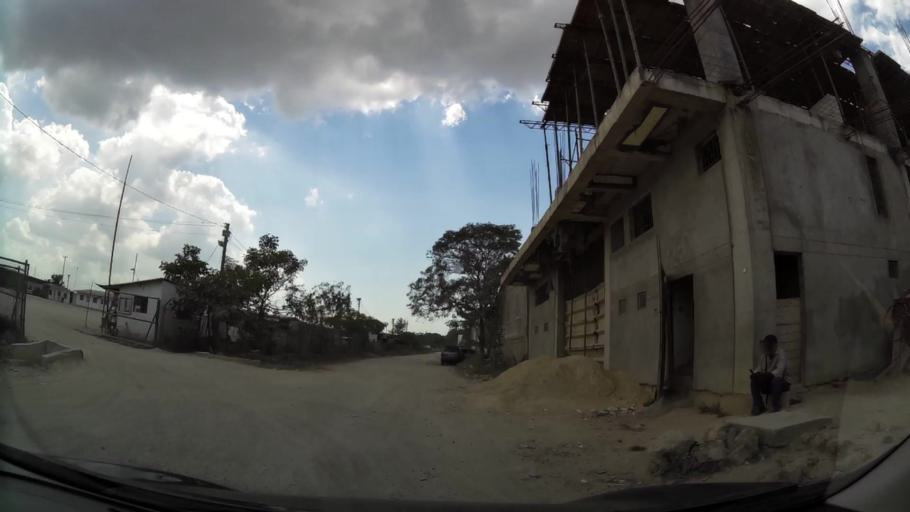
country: CO
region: Bolivar
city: Cartagena
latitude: 10.3729
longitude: -75.4576
